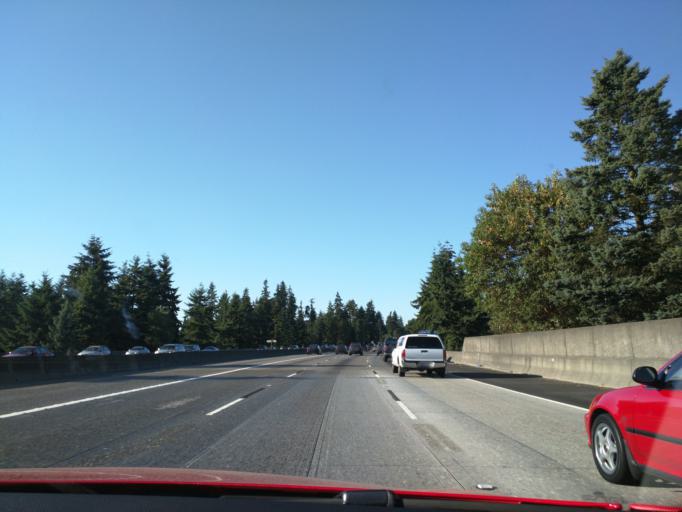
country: US
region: Washington
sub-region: King County
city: Shoreline
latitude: 47.7554
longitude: -122.3297
